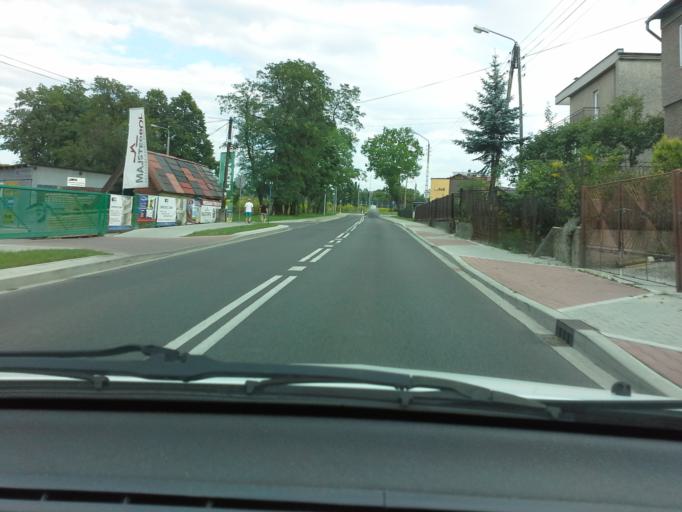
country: PL
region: Lesser Poland Voivodeship
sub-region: Powiat chrzanowski
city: Chrzanow
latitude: 50.1379
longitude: 19.4200
